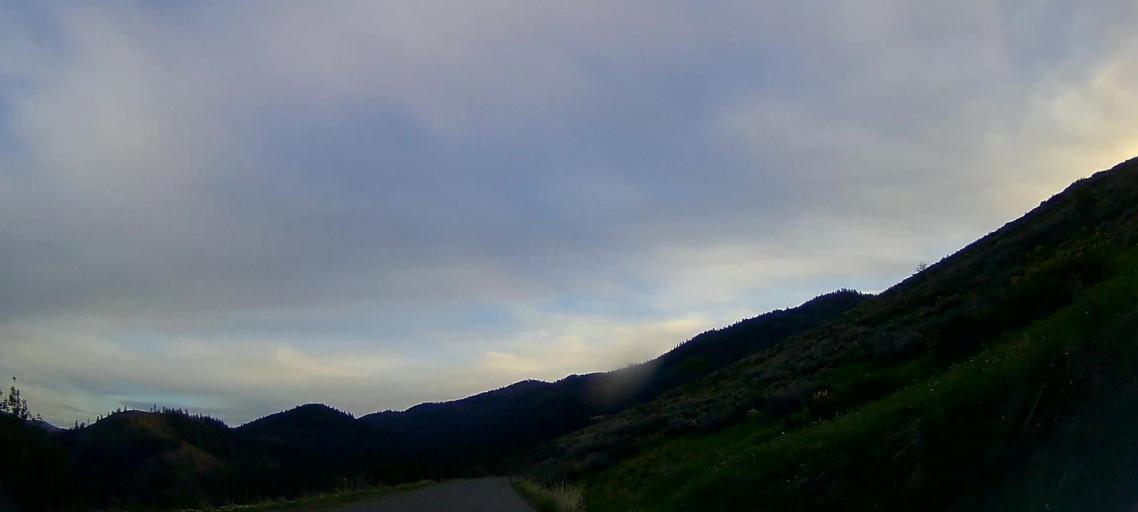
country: US
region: Washington
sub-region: Chelan County
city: Granite Falls
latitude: 48.4733
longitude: -120.2536
